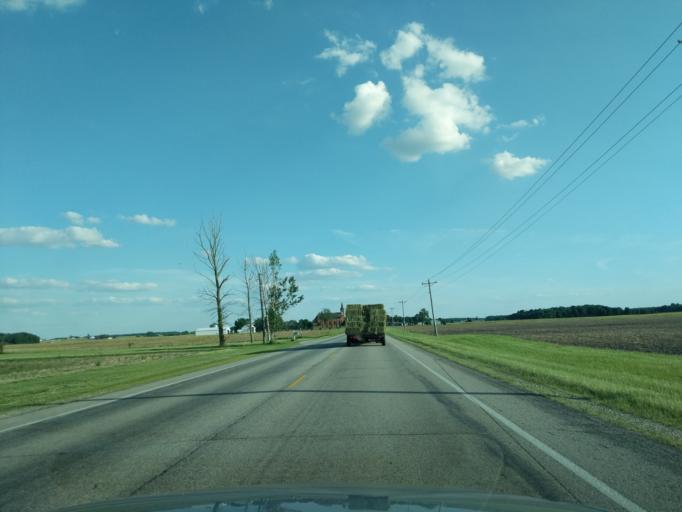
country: US
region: Indiana
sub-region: Huntington County
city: Roanoke
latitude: 41.0239
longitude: -85.4707
